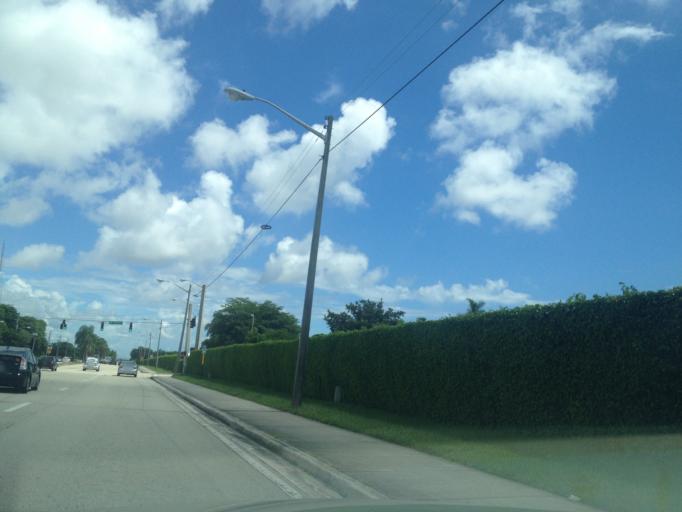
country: US
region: Florida
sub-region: Palm Beach County
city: Boynton Beach
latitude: 26.5156
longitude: -80.0901
